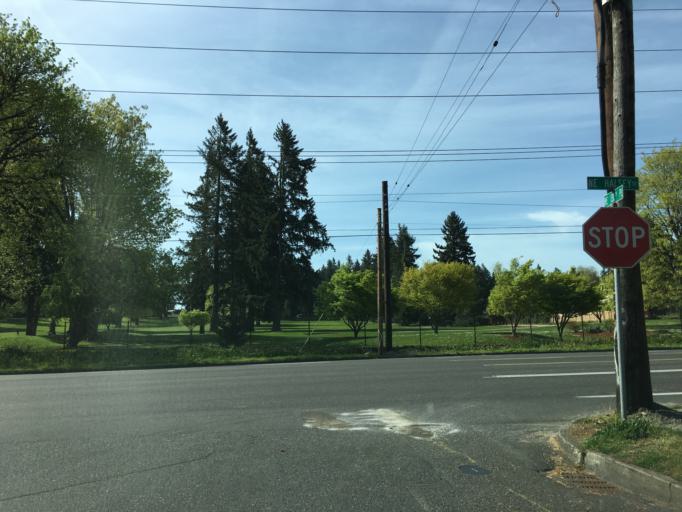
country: US
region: Oregon
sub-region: Multnomah County
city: Lents
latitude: 45.5338
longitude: -122.5205
